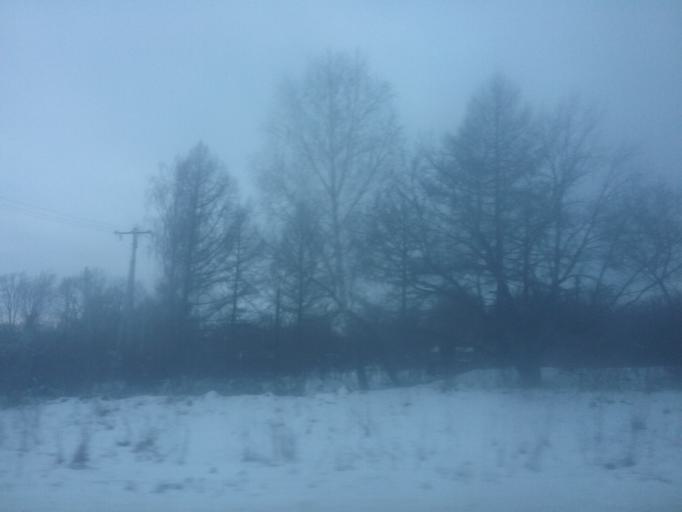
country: RU
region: Tula
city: Bogoroditsk
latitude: 53.7975
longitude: 38.1281
